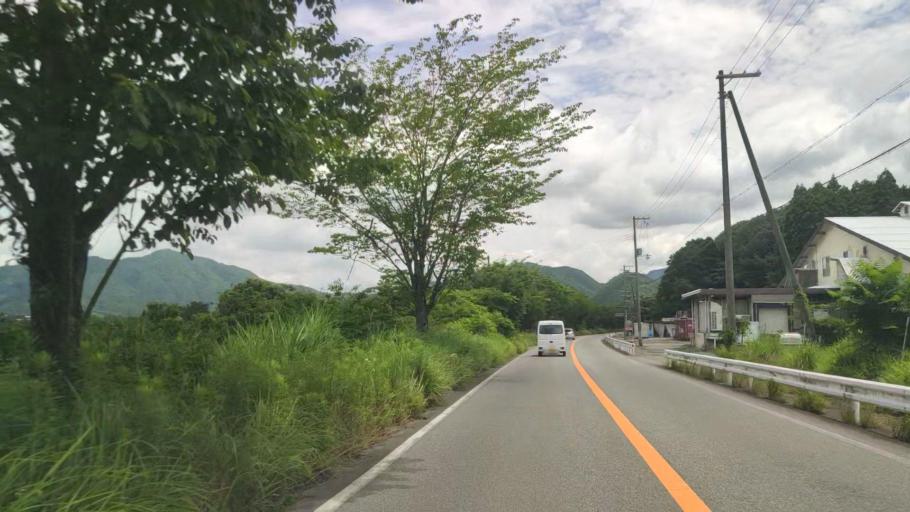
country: JP
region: Hyogo
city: Toyooka
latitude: 35.4150
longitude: 134.7870
